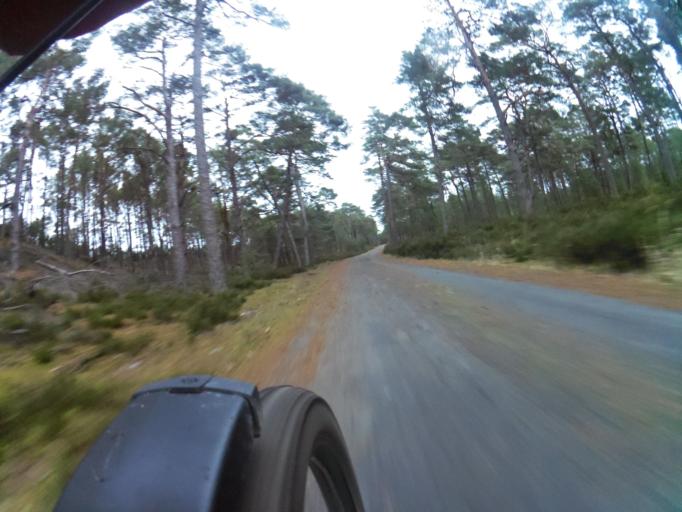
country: PL
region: Pomeranian Voivodeship
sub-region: Powiat wejherowski
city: Choczewo
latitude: 54.7937
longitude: 17.7630
